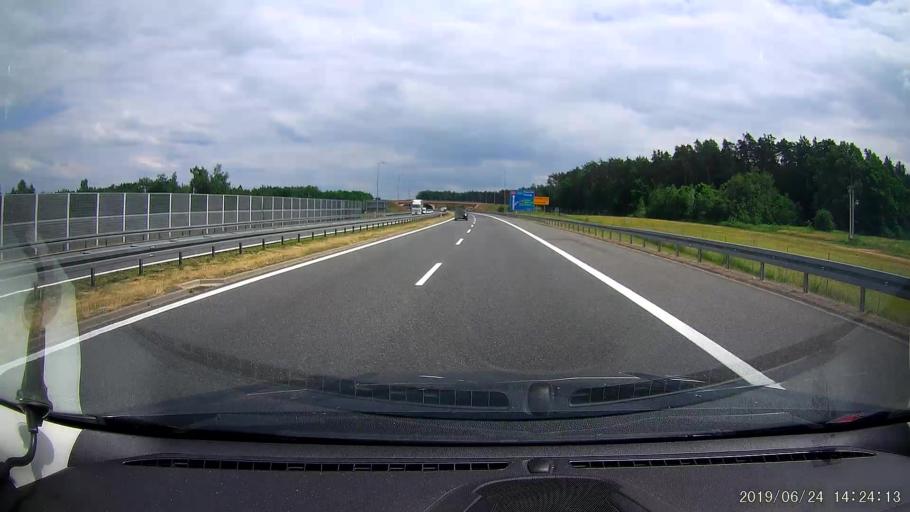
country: PL
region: Lesser Poland Voivodeship
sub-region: Powiat brzeski
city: Jasien
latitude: 49.9921
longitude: 20.5728
